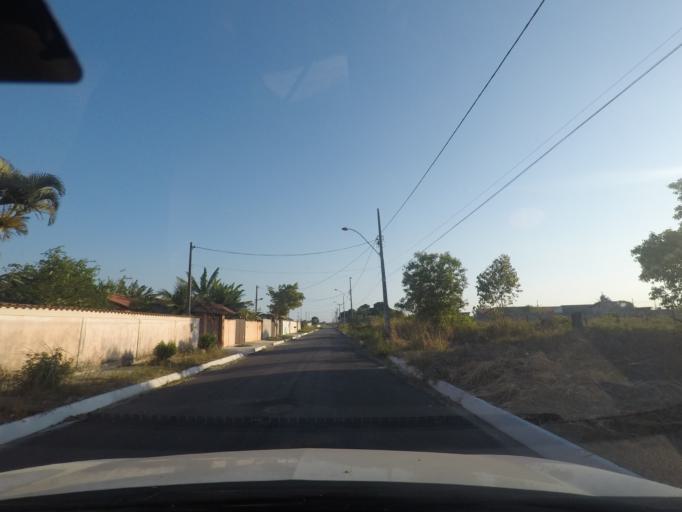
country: BR
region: Rio de Janeiro
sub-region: Marica
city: Marica
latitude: -22.9576
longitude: -42.9281
